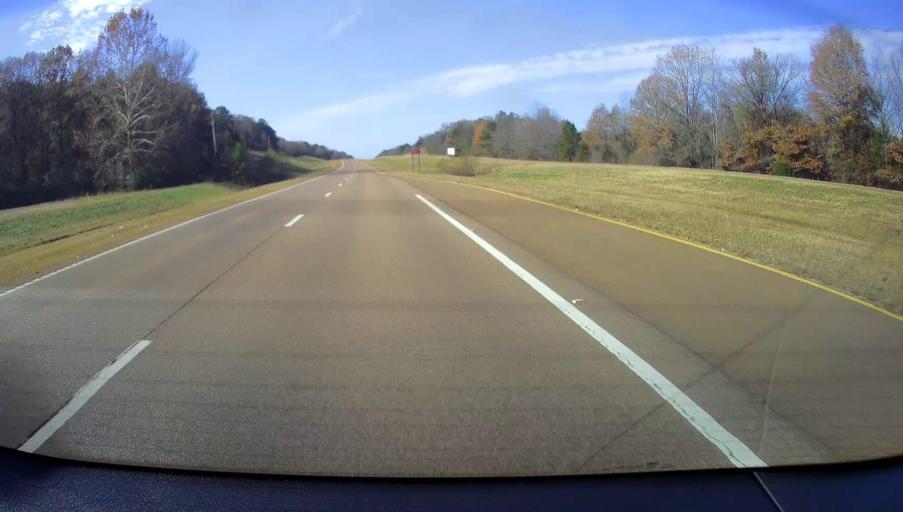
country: US
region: Mississippi
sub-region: Benton County
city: Ashland
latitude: 34.9463
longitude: -89.2330
